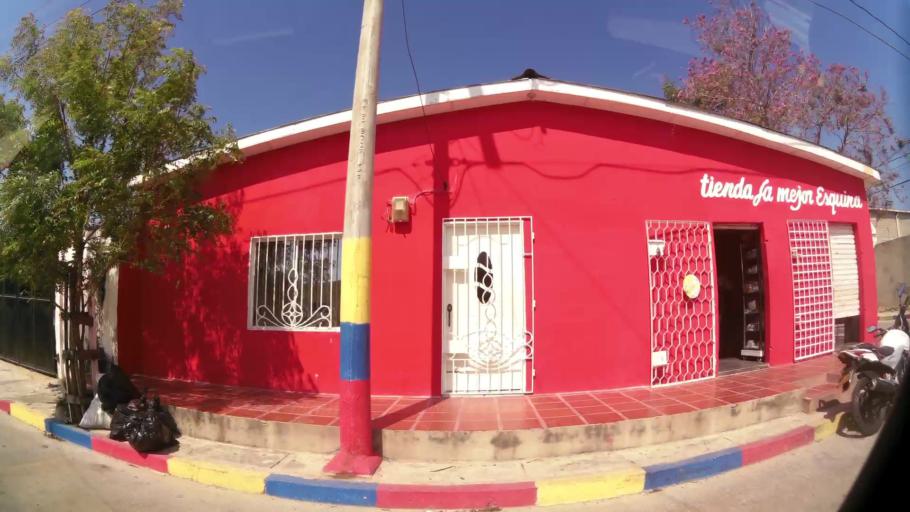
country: CO
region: Atlantico
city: Barranquilla
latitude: 10.9654
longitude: -74.8362
